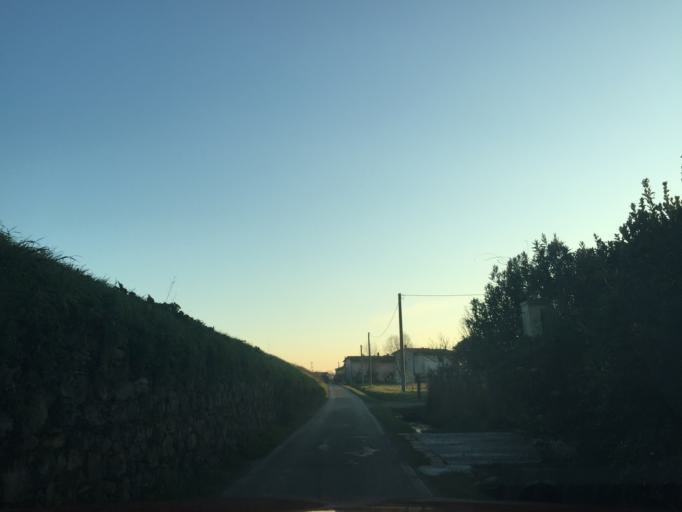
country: IT
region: Tuscany
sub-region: Provincia di Pistoia
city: Anchione
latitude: 43.8299
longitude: 10.7664
